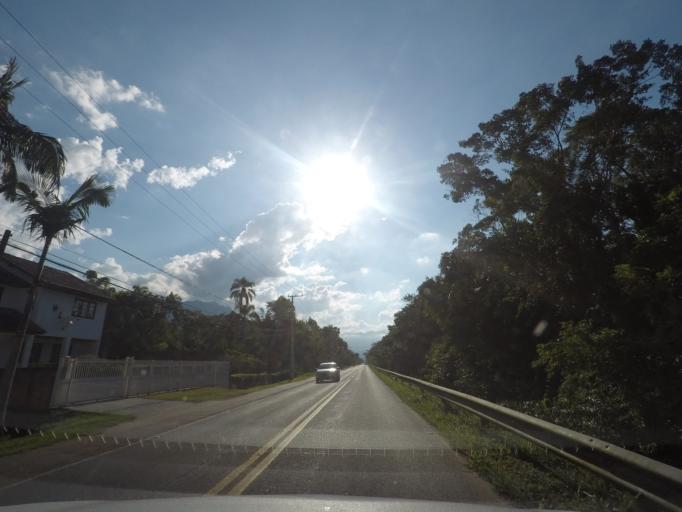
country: BR
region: Parana
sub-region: Antonina
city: Antonina
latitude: -25.4745
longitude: -48.8374
